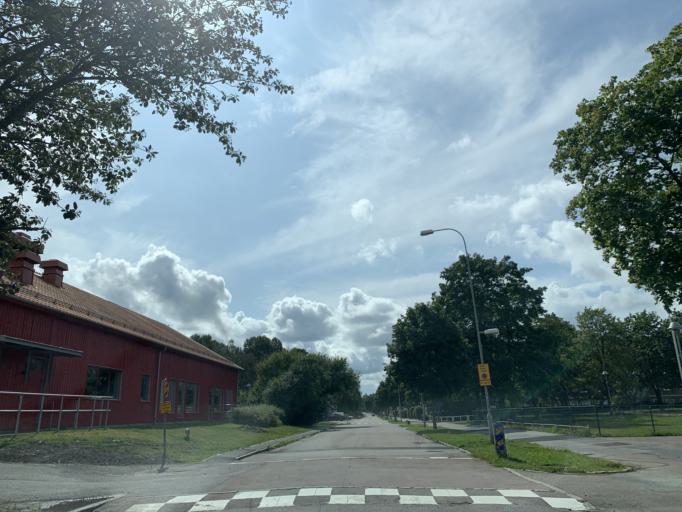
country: SE
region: Vaestra Goetaland
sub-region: Goteborg
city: Eriksbo
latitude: 57.7582
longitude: 12.0605
